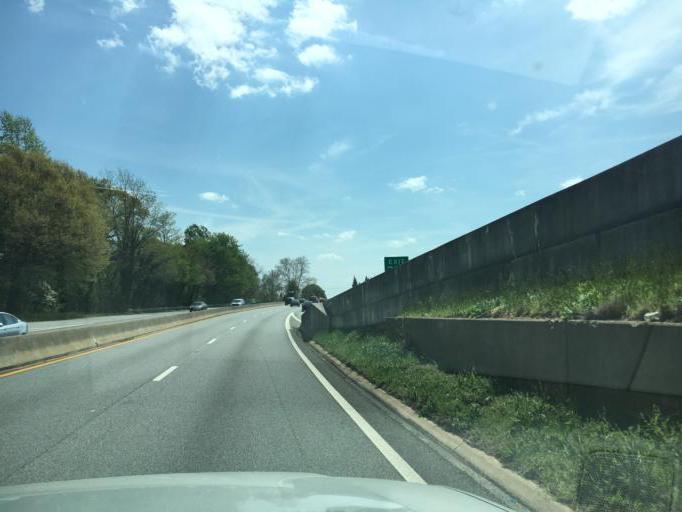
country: US
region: South Carolina
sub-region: Spartanburg County
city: Spartanburg
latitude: 34.9746
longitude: -81.9411
